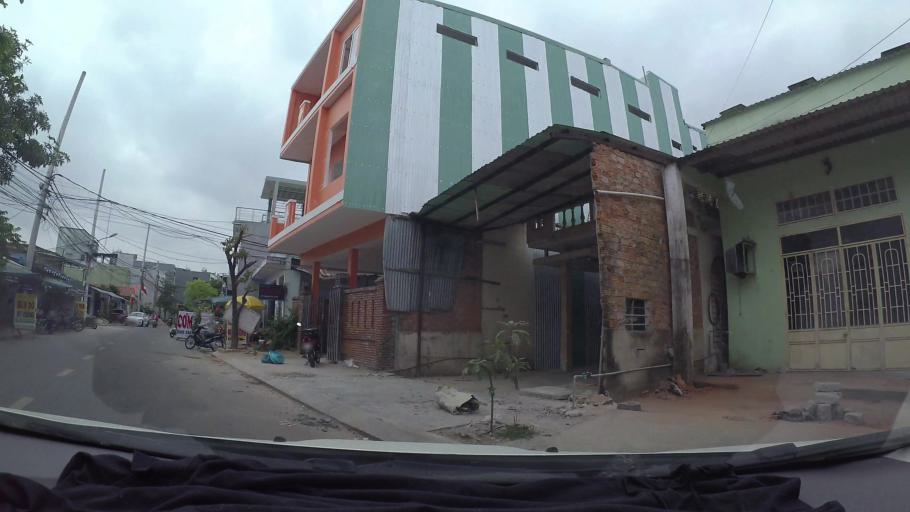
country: VN
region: Da Nang
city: Thanh Khe
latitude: 16.0624
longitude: 108.1761
